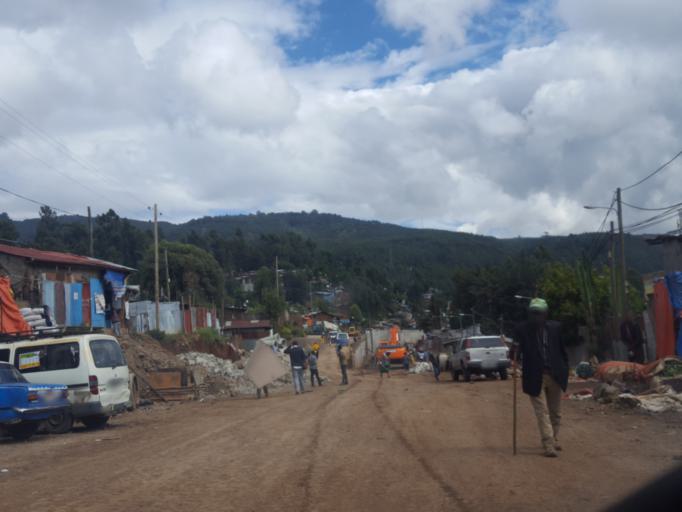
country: ET
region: Adis Abeba
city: Addis Ababa
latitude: 9.0652
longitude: 38.7625
